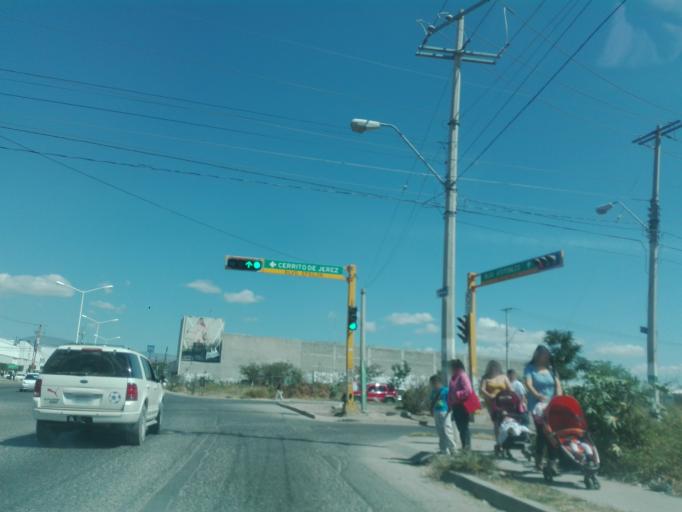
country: MX
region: Guanajuato
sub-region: Leon
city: San Jose de Duran (Los Troncoso)
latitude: 21.0835
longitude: -101.6270
